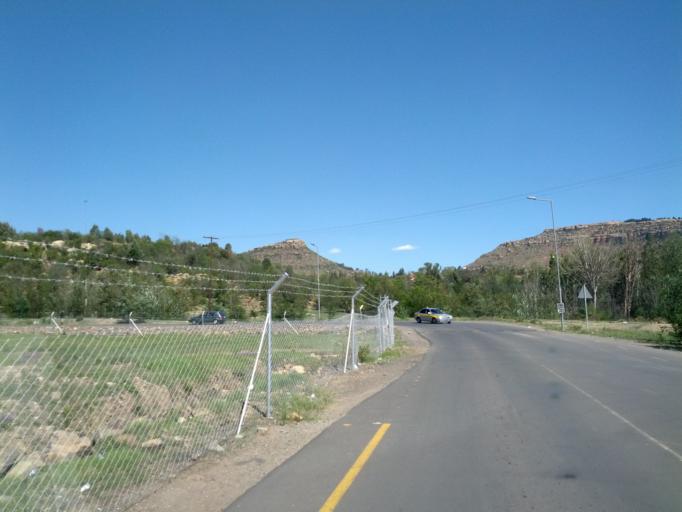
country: LS
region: Maseru
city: Maseru
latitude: -29.3186
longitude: 27.4748
